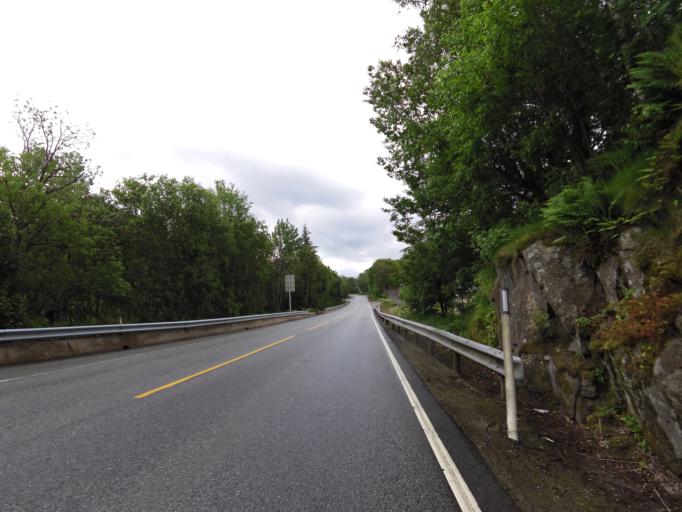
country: NO
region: Vest-Agder
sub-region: Farsund
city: Farsund
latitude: 58.0998
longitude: 6.8304
